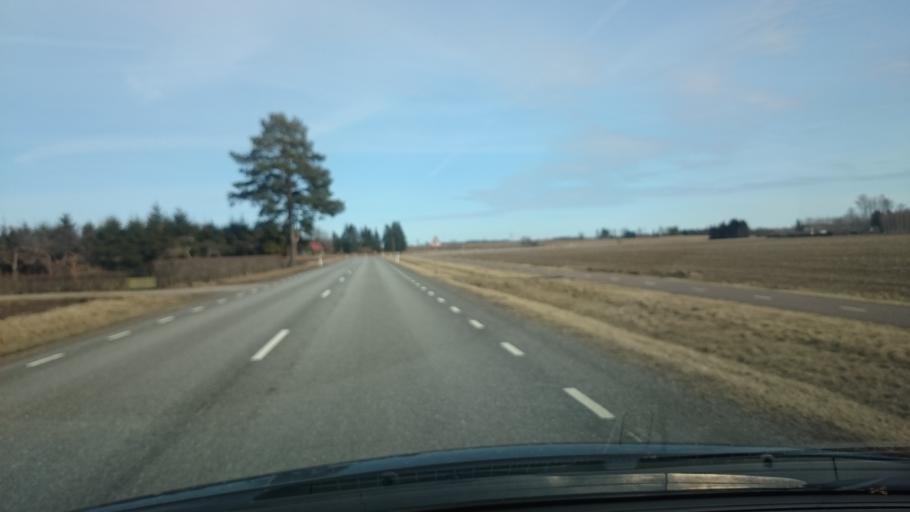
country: EE
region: Jaervamaa
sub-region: Paide linn
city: Paide
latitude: 58.8905
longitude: 25.4945
